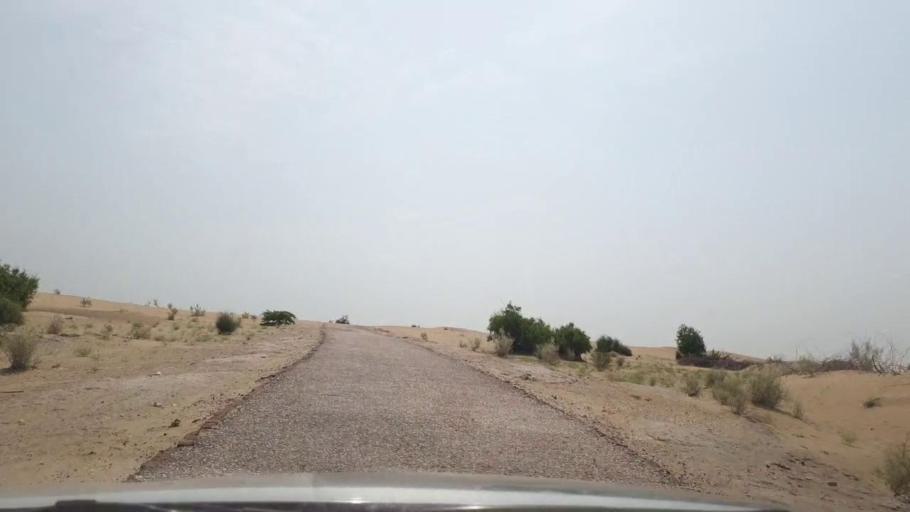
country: PK
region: Sindh
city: Pano Aqil
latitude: 27.6102
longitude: 69.1483
